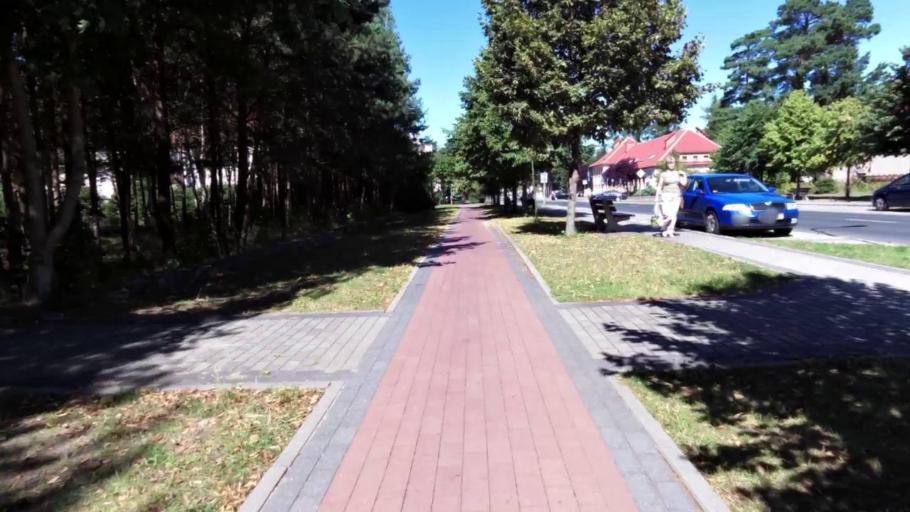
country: PL
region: West Pomeranian Voivodeship
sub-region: Powiat szczecinecki
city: Borne Sulinowo
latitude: 53.5828
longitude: 16.5428
